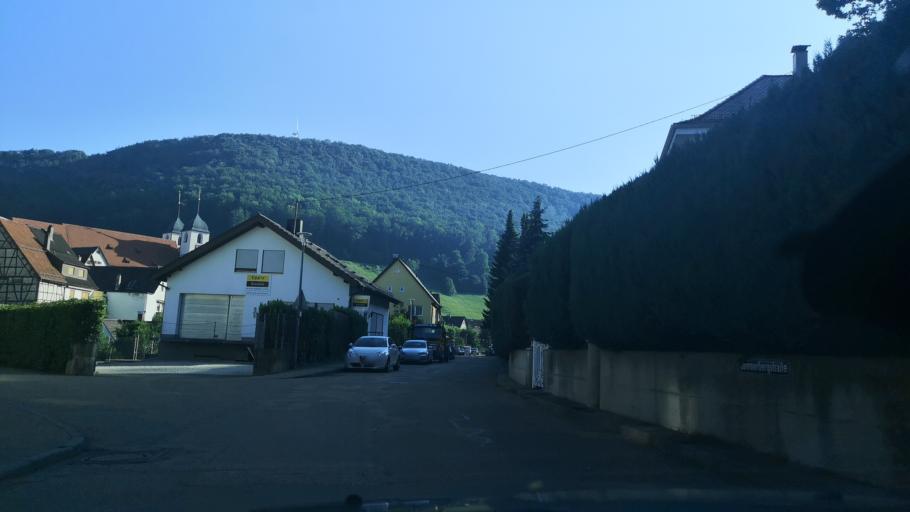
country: DE
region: Baden-Wuerttemberg
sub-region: Regierungsbezirk Stuttgart
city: Wiesensteig
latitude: 48.5638
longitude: 9.6267
